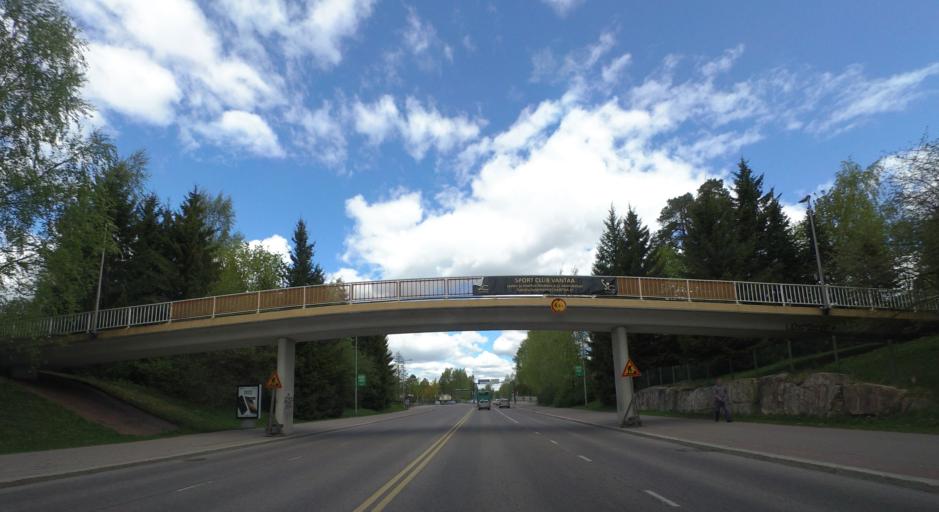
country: FI
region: Uusimaa
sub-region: Helsinki
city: Vantaa
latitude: 60.2982
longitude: 25.0344
